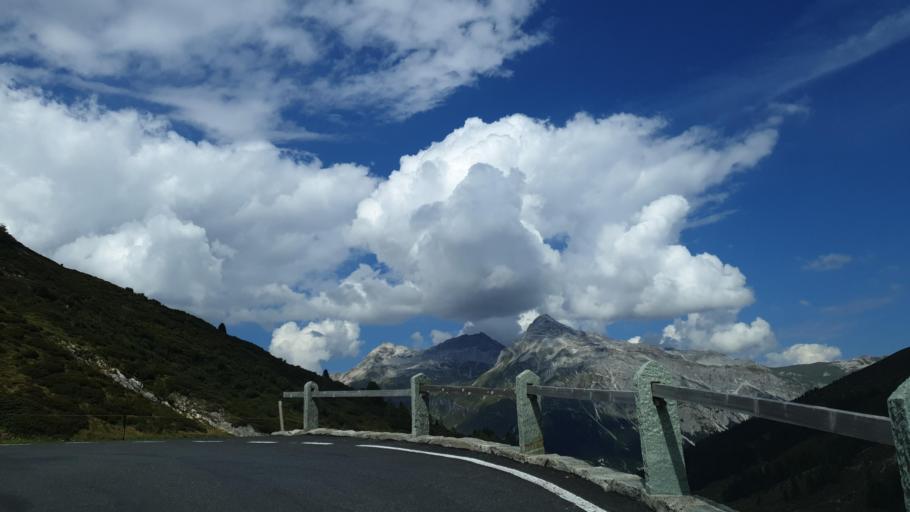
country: IT
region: Lombardy
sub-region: Provincia di Sondrio
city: Campodolcino
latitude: 46.5161
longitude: 9.3292
